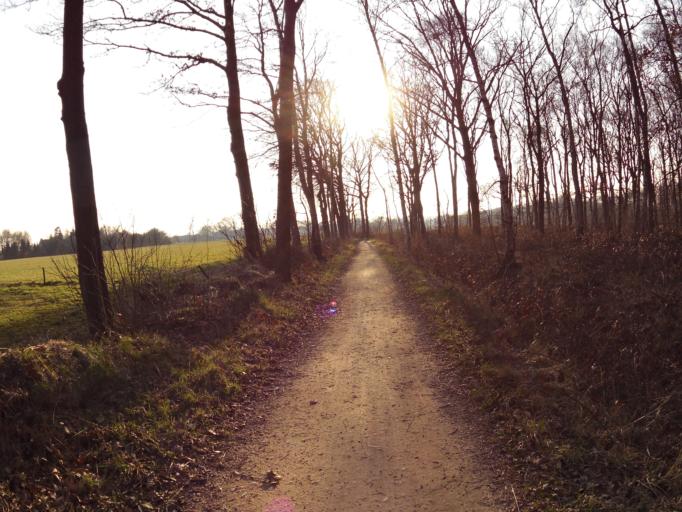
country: NL
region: North Brabant
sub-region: Gemeente Maasdonk
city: Geffen
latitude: 51.7042
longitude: 5.4035
